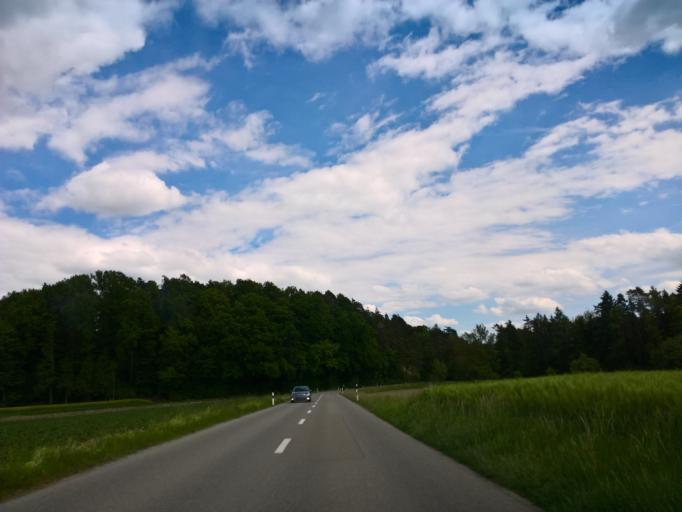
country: DE
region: Baden-Wuerttemberg
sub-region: Freiburg Region
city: Lottstetten
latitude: 47.6000
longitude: 8.6051
